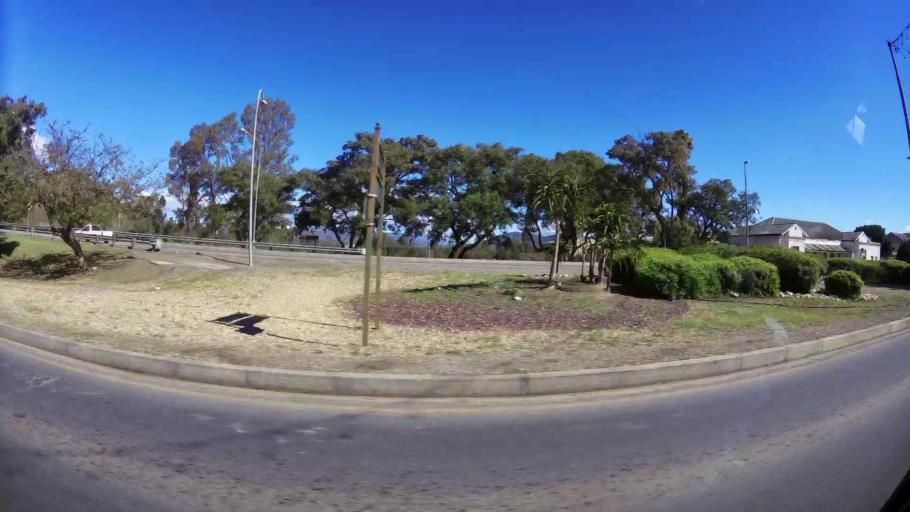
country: ZA
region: Western Cape
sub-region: Cape Winelands District Municipality
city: Ashton
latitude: -33.8094
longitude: 19.8793
